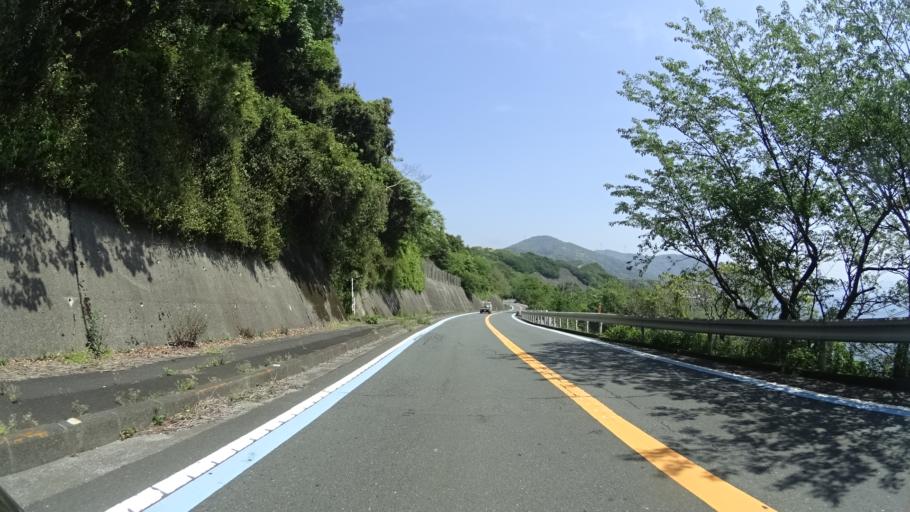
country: JP
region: Ehime
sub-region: Nishiuwa-gun
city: Ikata-cho
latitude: 33.4000
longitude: 132.1654
